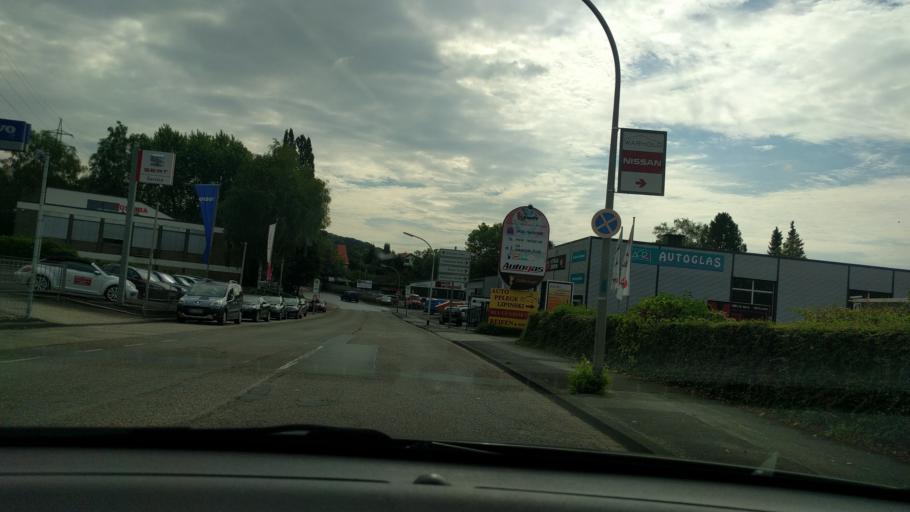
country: DE
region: North Rhine-Westphalia
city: Witten
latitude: 51.4552
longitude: 7.3549
